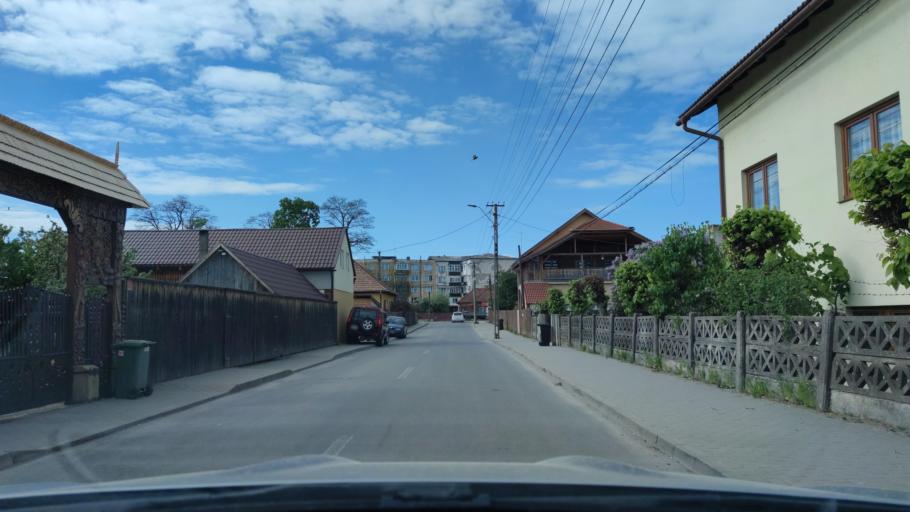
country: RO
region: Harghita
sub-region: Municipiul Gheorgheni
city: Gheorgheni
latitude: 46.7249
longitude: 25.5934
